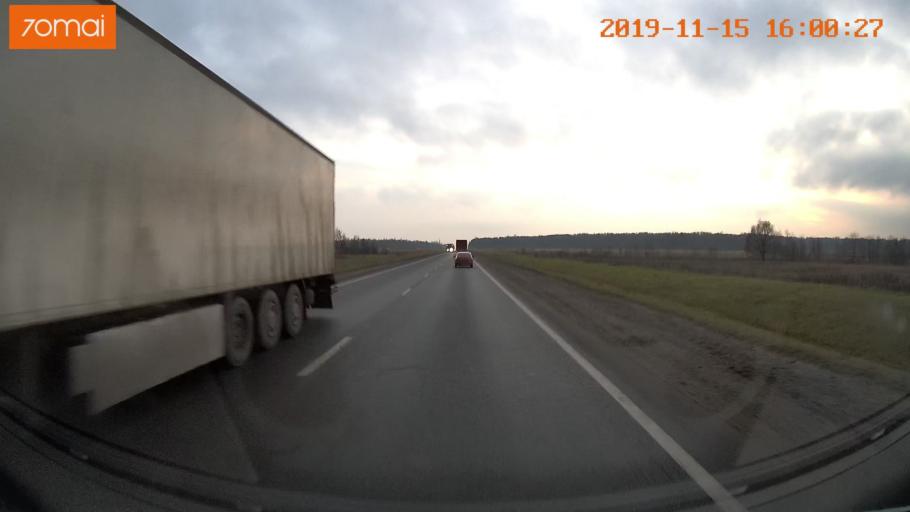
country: RU
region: Jaroslavl
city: Yaroslavl
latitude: 57.7958
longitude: 39.9387
